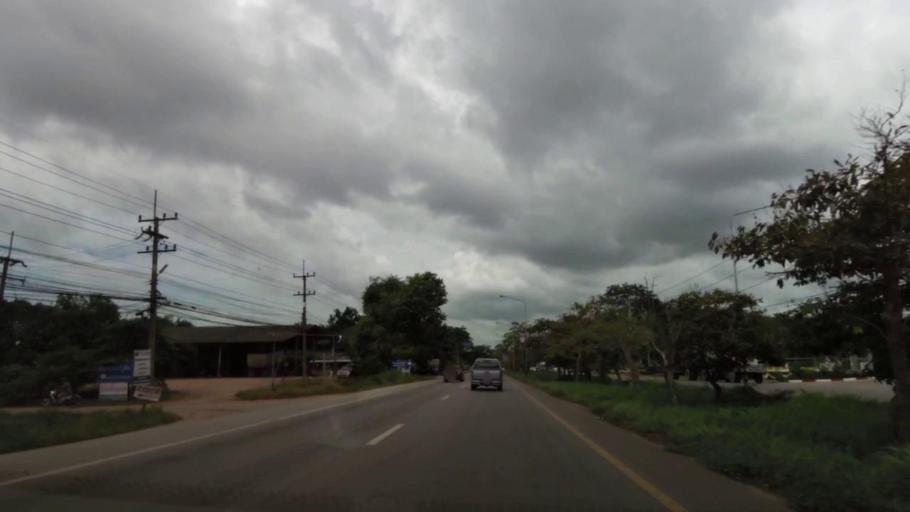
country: TH
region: Rayong
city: Klaeng
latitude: 12.7764
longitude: 101.7191
